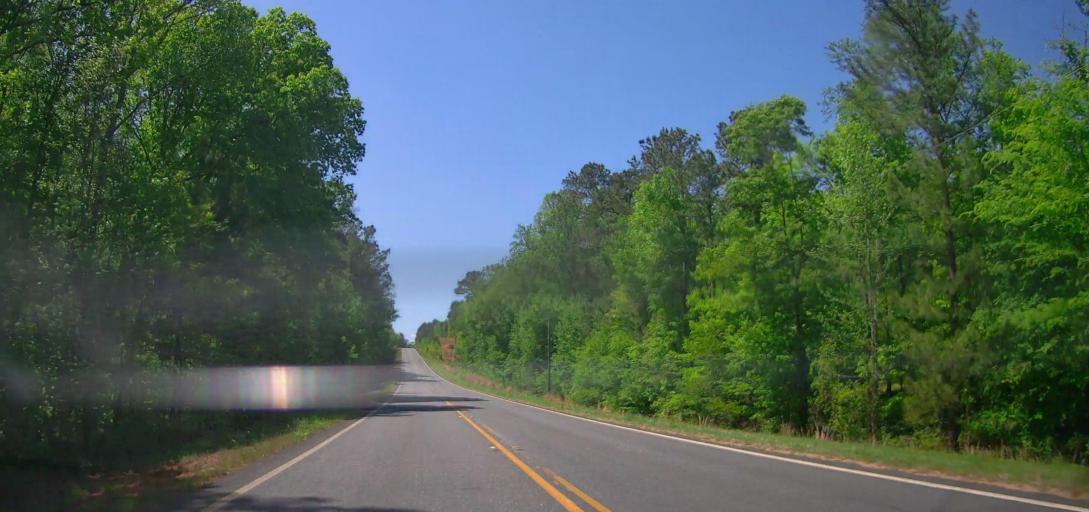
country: US
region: Georgia
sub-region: Putnam County
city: Eatonton
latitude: 33.2057
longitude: -83.4656
